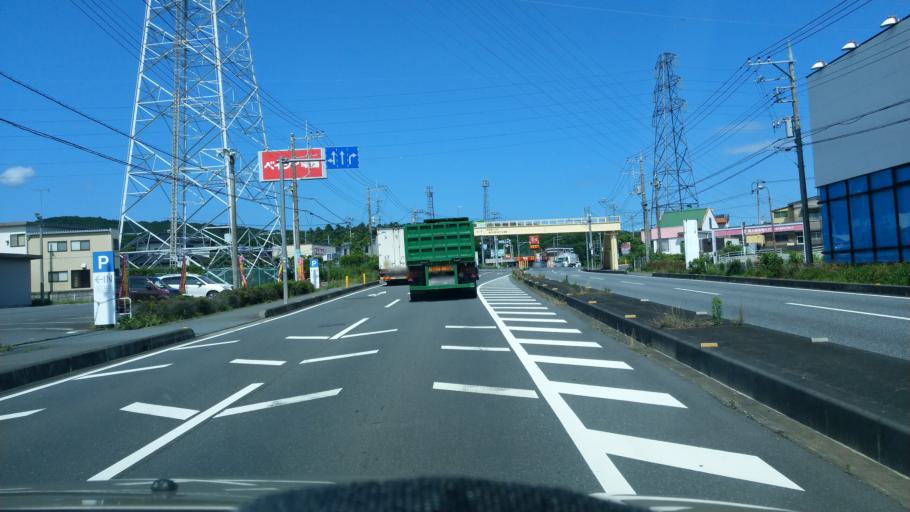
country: JP
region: Saitama
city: Ogawa
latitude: 36.0391
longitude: 139.3196
